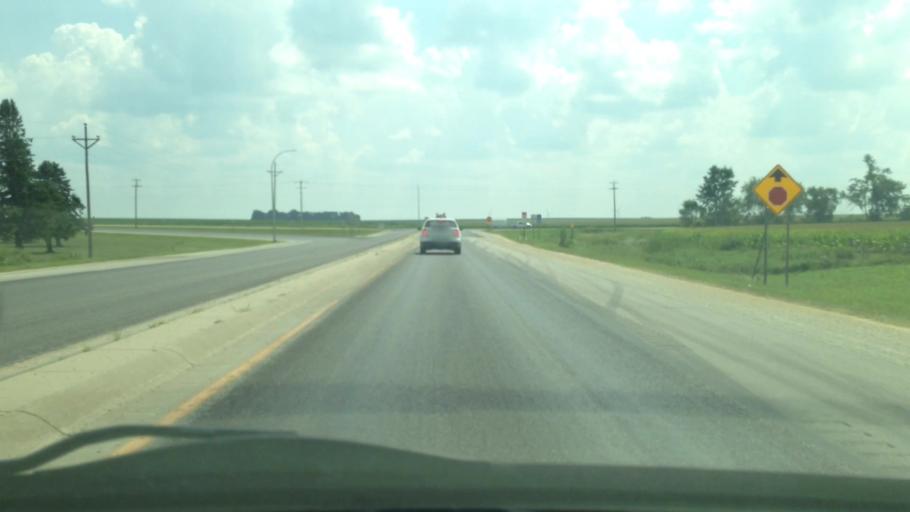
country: US
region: Minnesota
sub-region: Mower County
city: Grand Meadow
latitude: 43.7129
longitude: -92.4795
